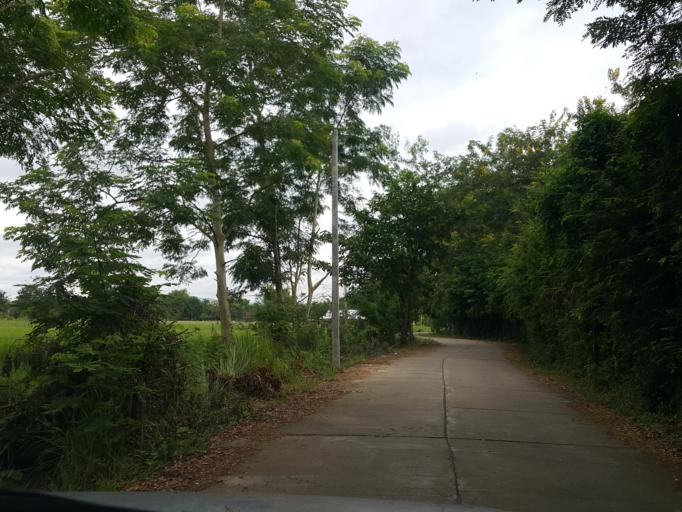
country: TH
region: Chiang Mai
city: San Sai
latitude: 18.8227
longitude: 99.1116
